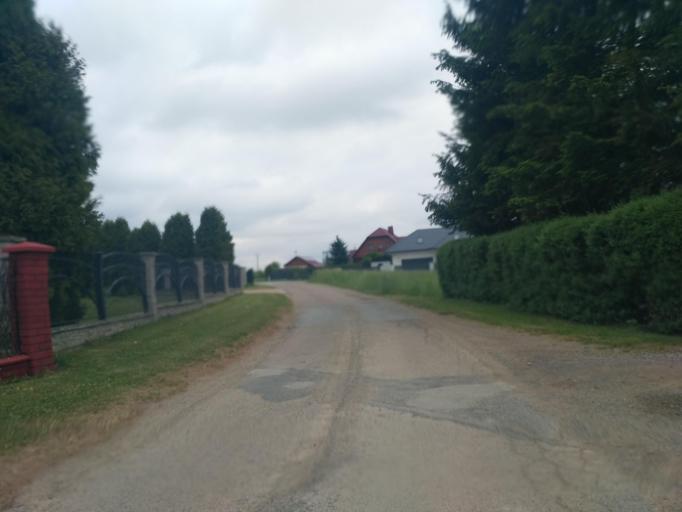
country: PL
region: Subcarpathian Voivodeship
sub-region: Powiat krosnienski
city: Chorkowka
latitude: 49.6610
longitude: 21.7200
